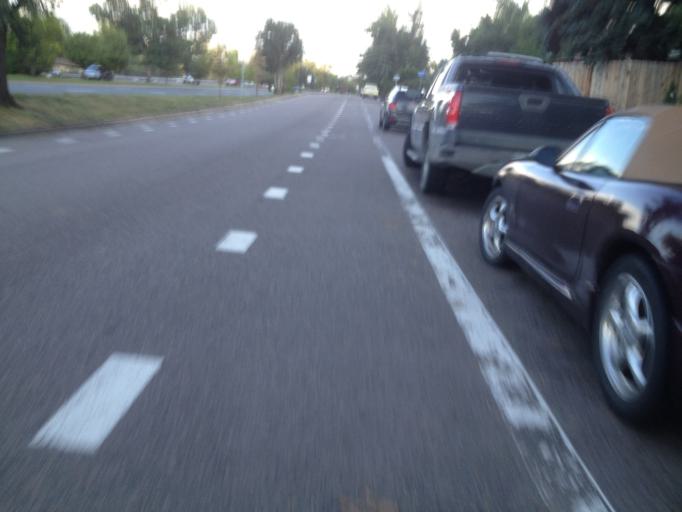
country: US
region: Colorado
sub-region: Boulder County
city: Boulder
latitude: 39.9879
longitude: -105.2536
